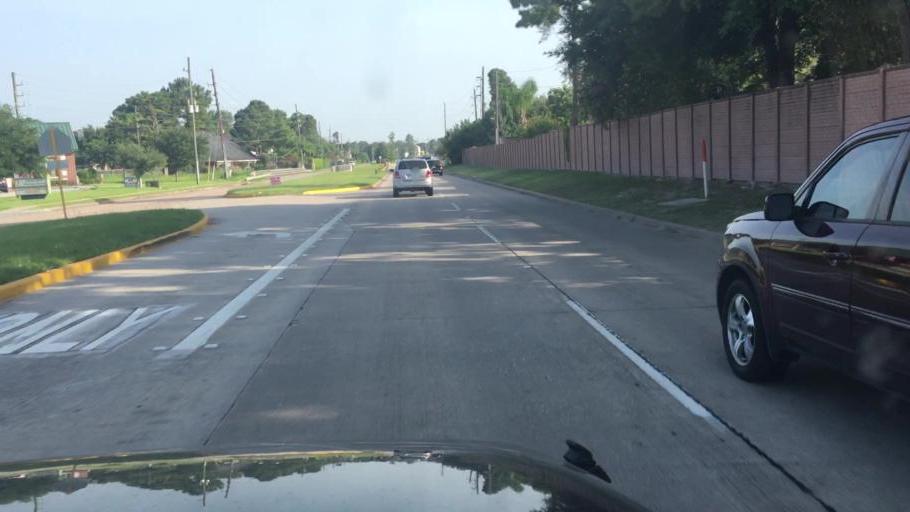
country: US
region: Texas
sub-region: Harris County
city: Atascocita
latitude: 29.9903
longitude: -95.1618
